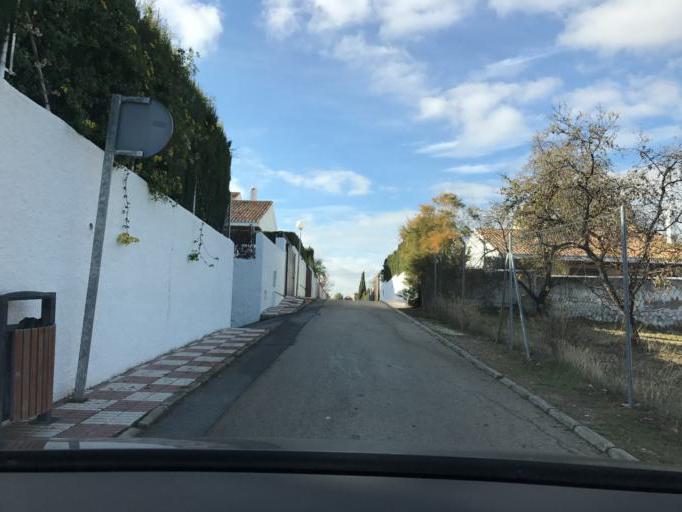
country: ES
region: Andalusia
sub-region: Provincia de Granada
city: Otura
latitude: 37.0840
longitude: -3.6225
